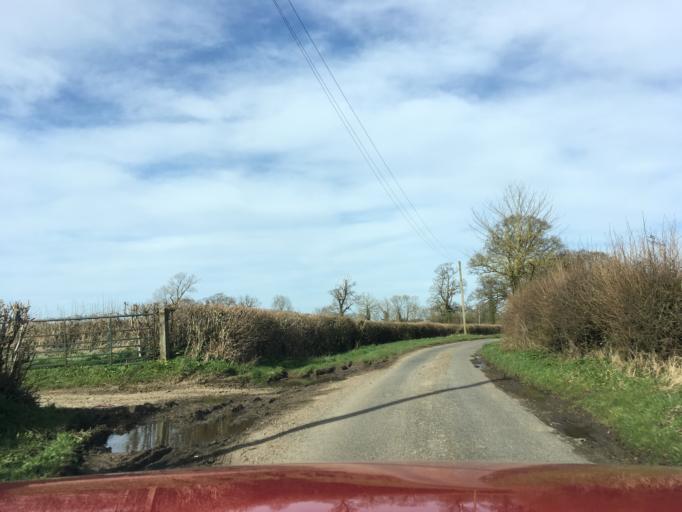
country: GB
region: England
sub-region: Wiltshire
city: Luckington
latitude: 51.5285
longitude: -2.2463
